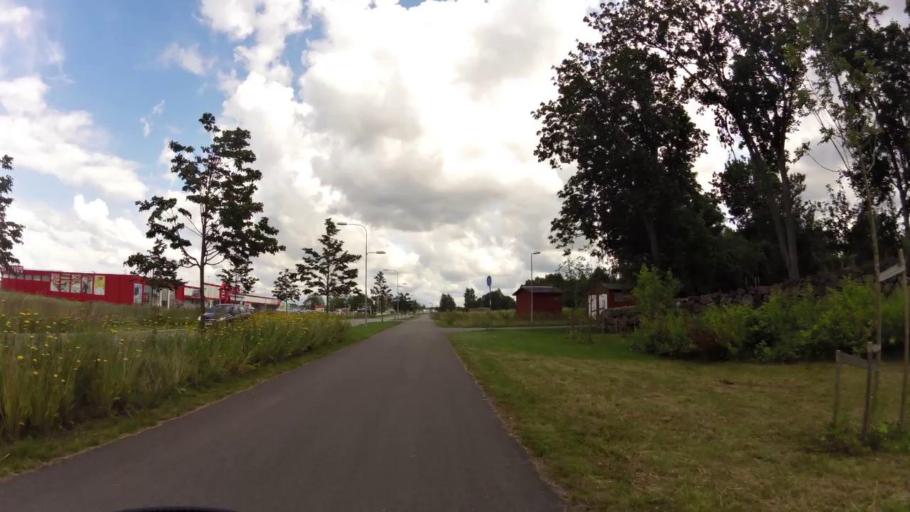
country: SE
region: OEstergoetland
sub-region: Linkopings Kommun
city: Linkoping
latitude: 58.4326
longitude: 15.6047
